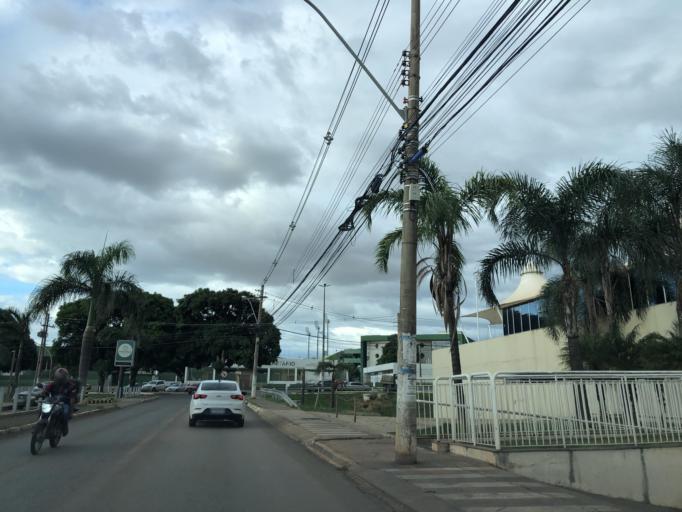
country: BR
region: Goias
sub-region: Luziania
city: Luziania
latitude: -16.0143
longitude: -48.0618
